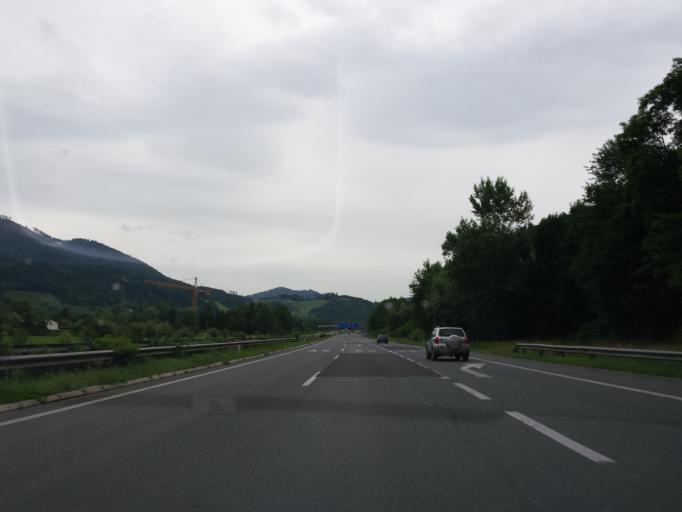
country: AT
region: Styria
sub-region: Politischer Bezirk Graz-Umgebung
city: Deutschfeistritz
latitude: 47.1717
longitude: 15.3325
